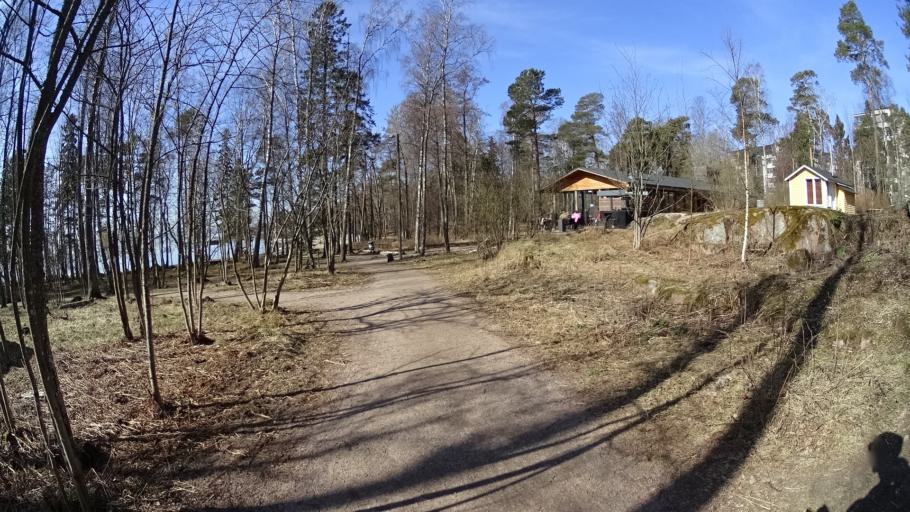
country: FI
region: Uusimaa
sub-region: Helsinki
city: Helsinki
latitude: 60.1467
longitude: 24.8841
